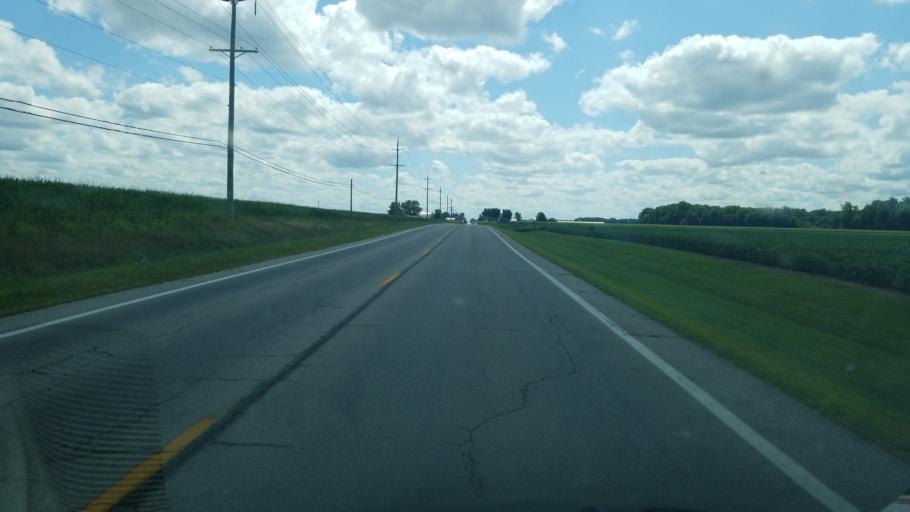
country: US
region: Ohio
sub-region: Henry County
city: Napoleon
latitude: 41.3758
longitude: -84.1206
